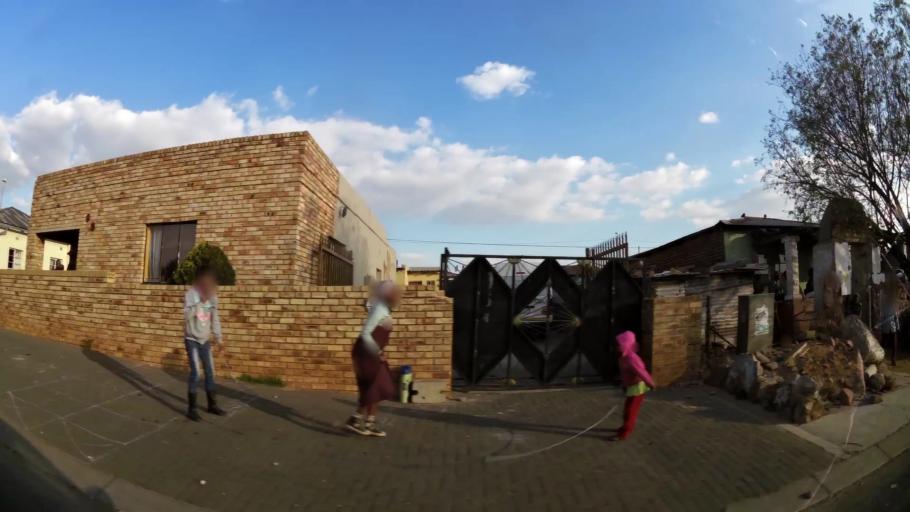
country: ZA
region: Gauteng
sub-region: West Rand District Municipality
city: Krugersdorp
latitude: -26.0716
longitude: 27.7574
